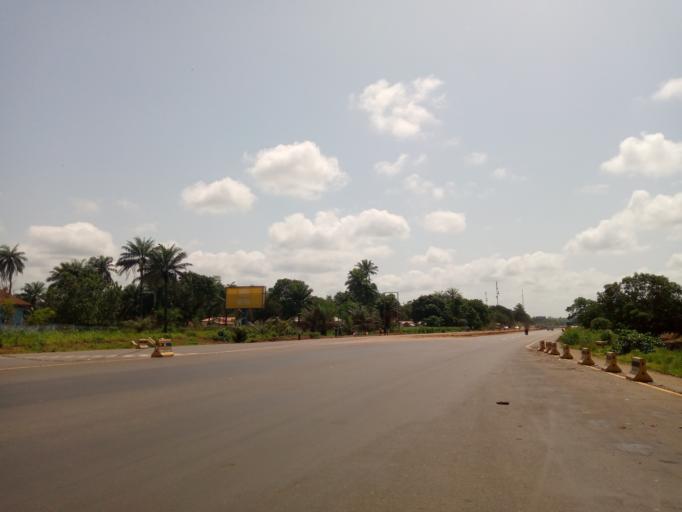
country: SL
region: Western Area
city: Waterloo
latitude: 8.3868
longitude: -12.9509
